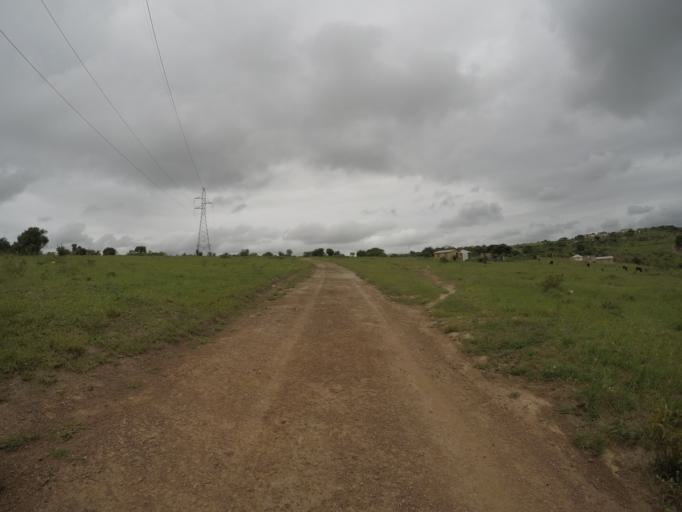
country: ZA
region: KwaZulu-Natal
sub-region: uThungulu District Municipality
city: Empangeni
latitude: -28.6001
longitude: 31.8465
